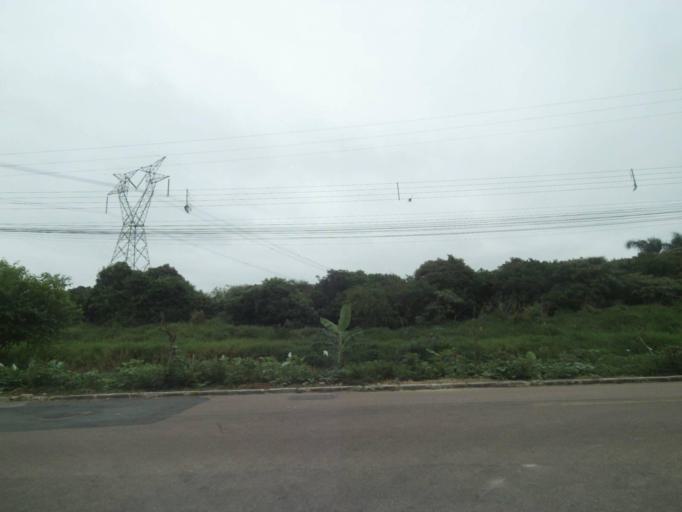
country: BR
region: Parana
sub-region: Araucaria
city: Araucaria
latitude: -25.5429
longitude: -49.3441
